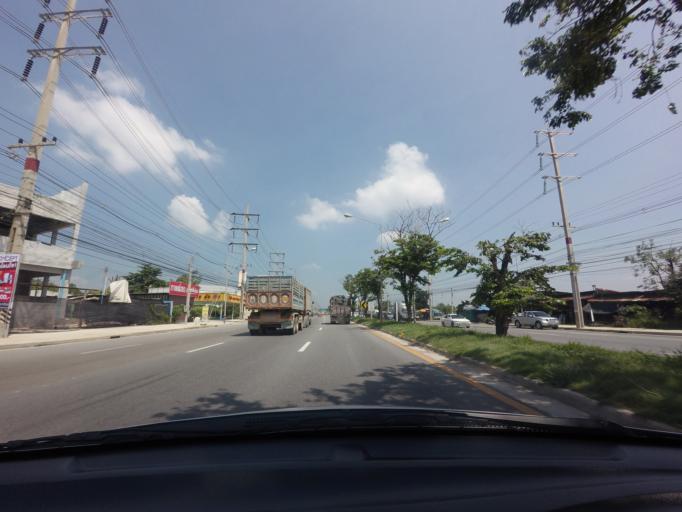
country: TH
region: Chachoengsao
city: Chachoengsao
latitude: 13.6476
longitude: 101.0461
